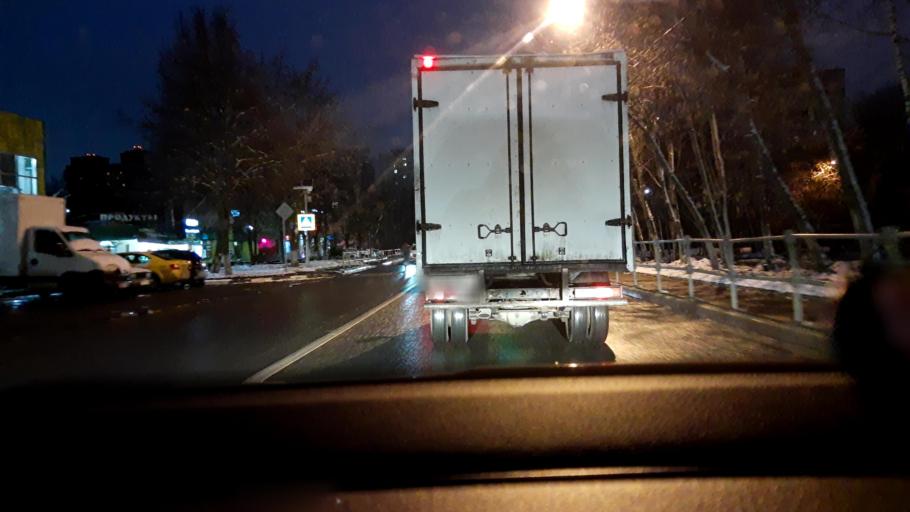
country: RU
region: Moskovskaya
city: Dolgoprudnyy
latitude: 55.9434
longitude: 37.4918
